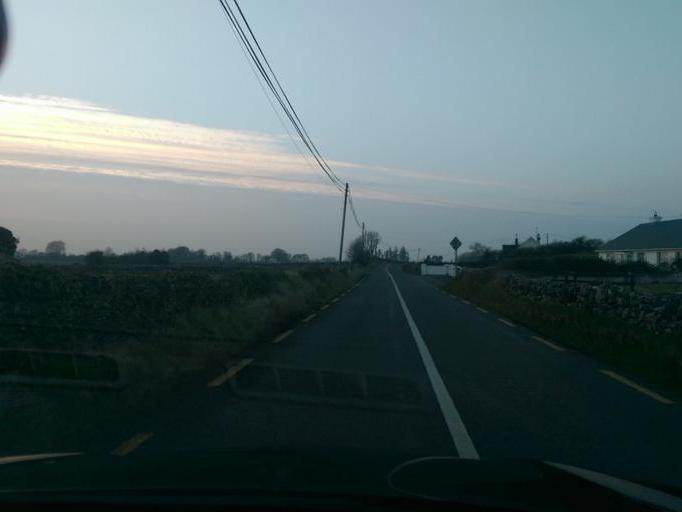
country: IE
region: Connaught
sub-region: County Galway
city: Loughrea
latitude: 53.2190
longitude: -8.6211
